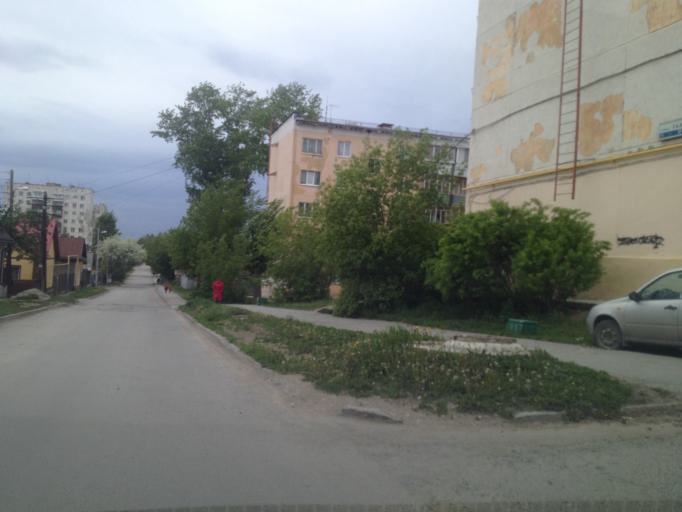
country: RU
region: Sverdlovsk
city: Sovkhoznyy
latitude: 56.7627
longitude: 60.6040
